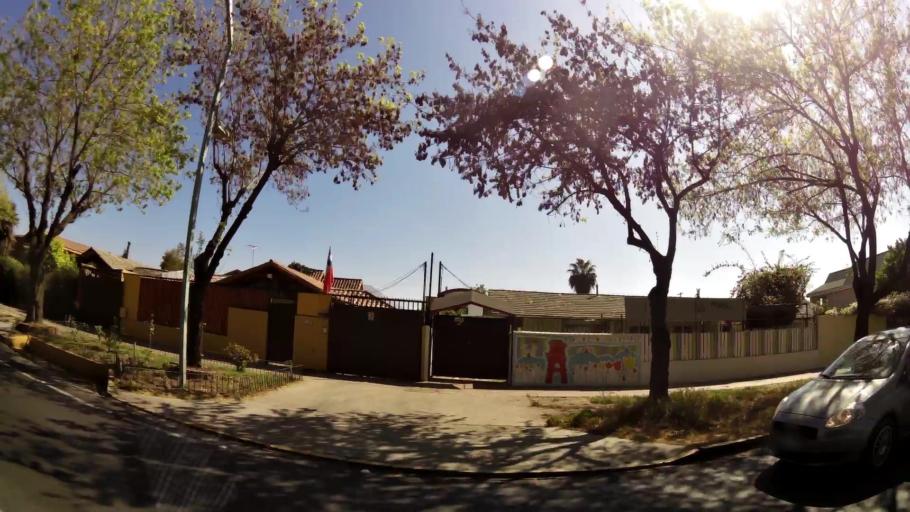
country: CL
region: Santiago Metropolitan
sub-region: Provincia de Santiago
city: Villa Presidente Frei, Nunoa, Santiago, Chile
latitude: -33.4178
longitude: -70.5503
